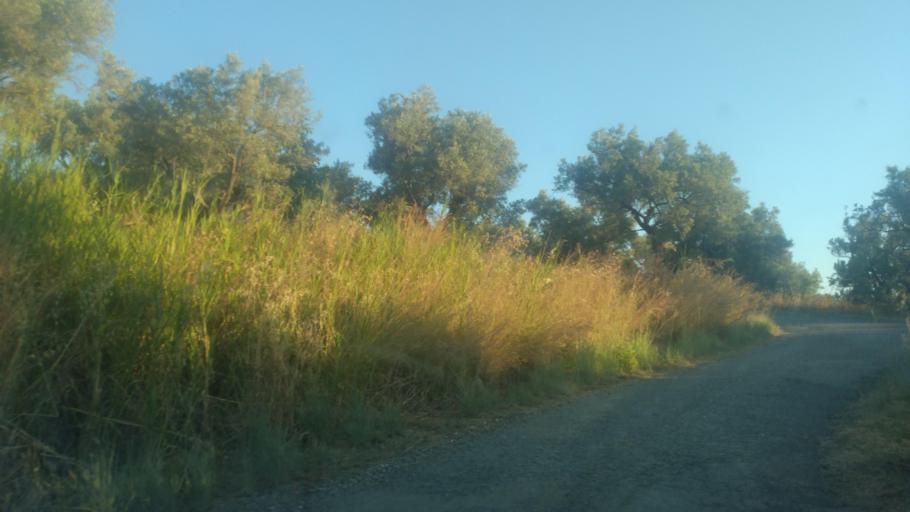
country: IT
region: Calabria
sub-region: Provincia di Catanzaro
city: Staletti
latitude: 38.7733
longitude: 16.5483
